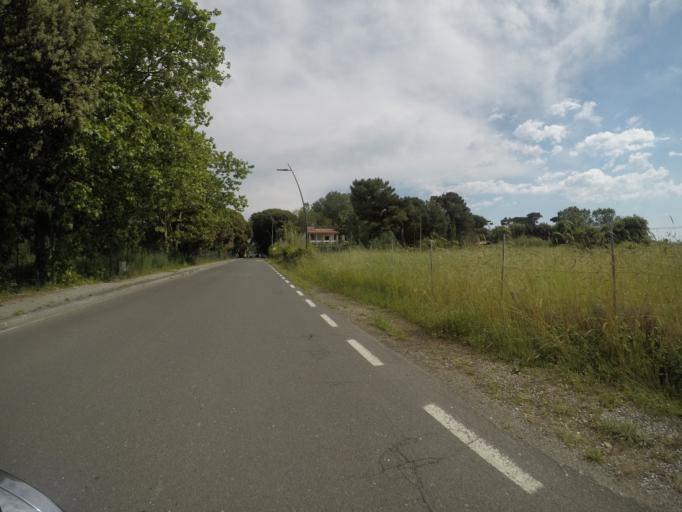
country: IT
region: Tuscany
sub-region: Provincia di Massa-Carrara
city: Capanne-Prato-Cinquale
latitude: 43.9744
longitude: 10.1510
